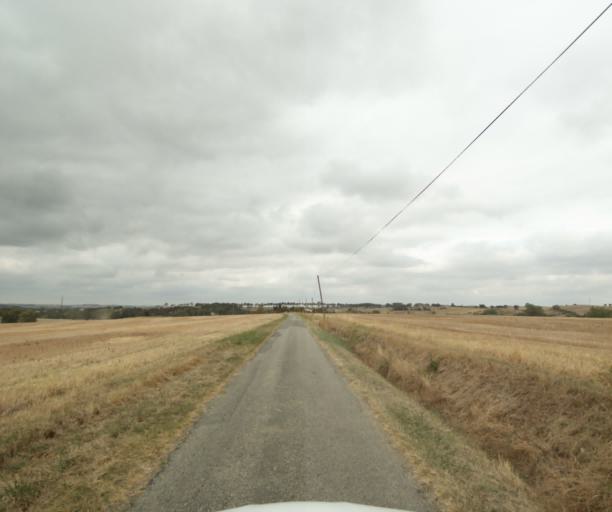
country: FR
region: Midi-Pyrenees
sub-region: Departement de la Haute-Garonne
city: Villefranche-de-Lauragais
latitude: 43.4095
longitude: 1.7305
